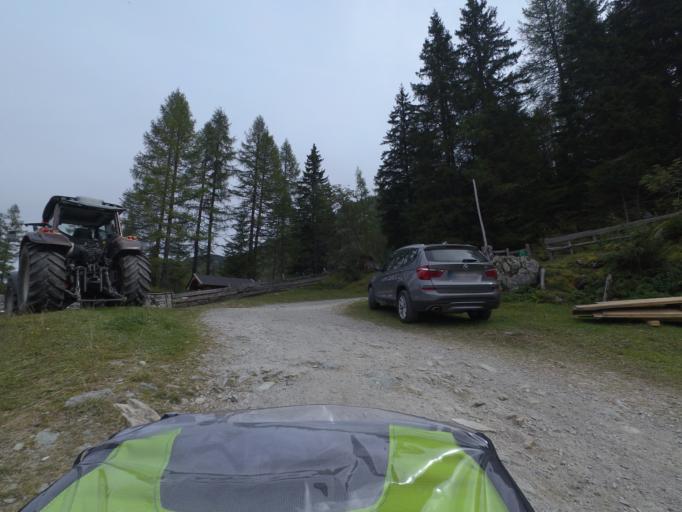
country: AT
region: Salzburg
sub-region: Politischer Bezirk Sankt Johann im Pongau
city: Untertauern
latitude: 47.2915
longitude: 13.5780
